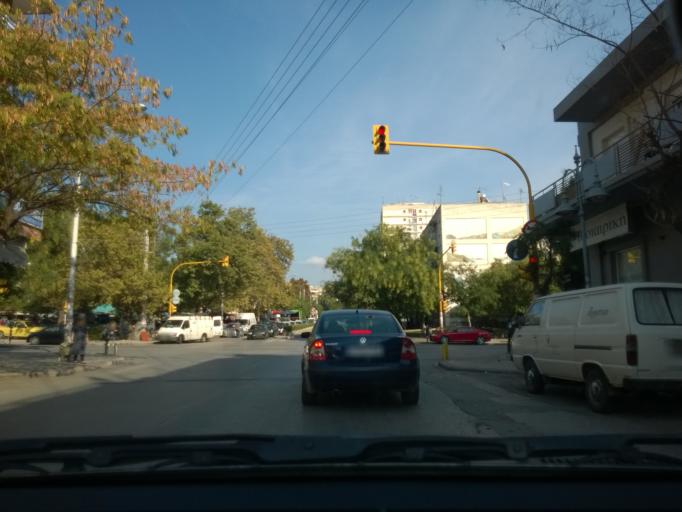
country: GR
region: Central Macedonia
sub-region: Nomos Thessalonikis
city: Thessaloniki
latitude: 40.6484
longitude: 22.9309
